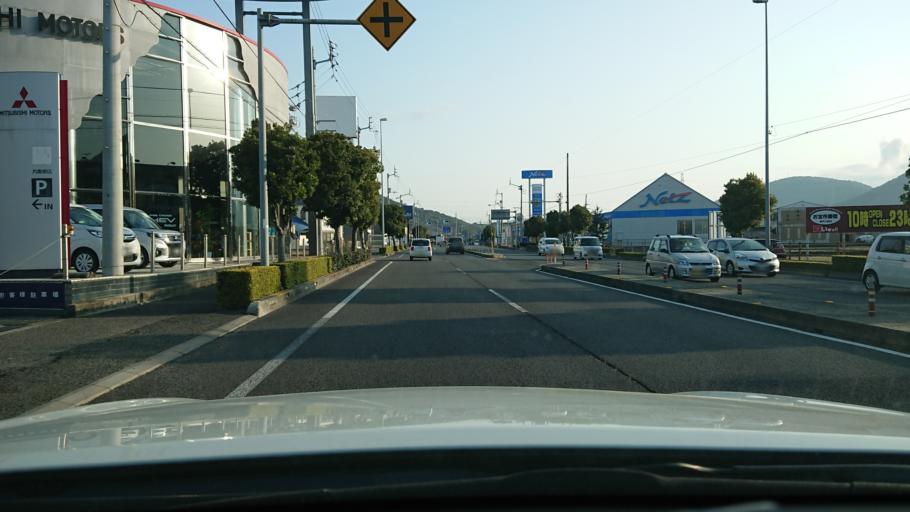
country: JP
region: Kagawa
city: Sakaidecho
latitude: 34.2931
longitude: 133.8347
